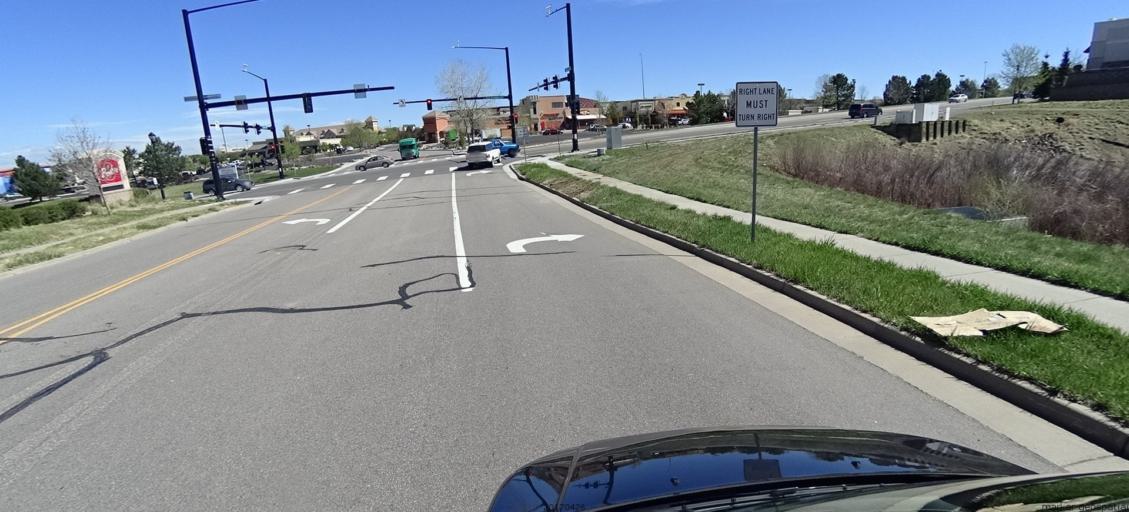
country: US
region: Colorado
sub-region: Adams County
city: Lone Tree
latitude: 39.5533
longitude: -104.8805
